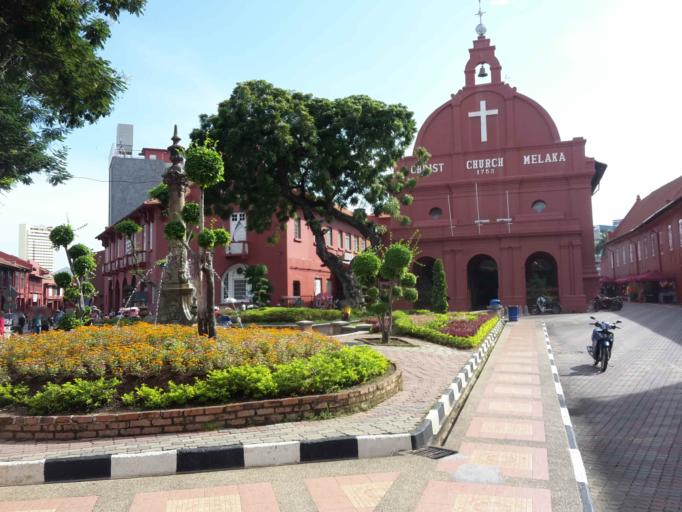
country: MY
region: Melaka
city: Malacca
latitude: 2.1943
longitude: 102.2489
